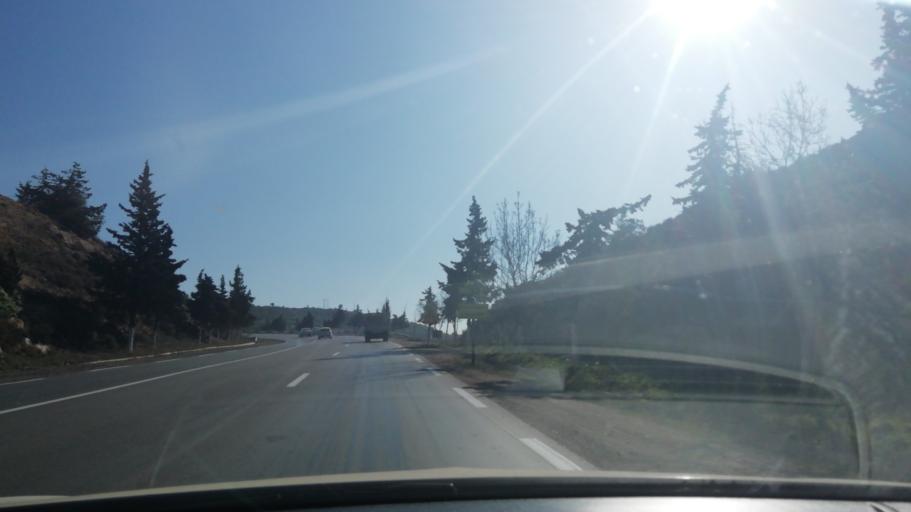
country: DZ
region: Tlemcen
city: Nedroma
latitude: 35.0890
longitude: -1.8182
